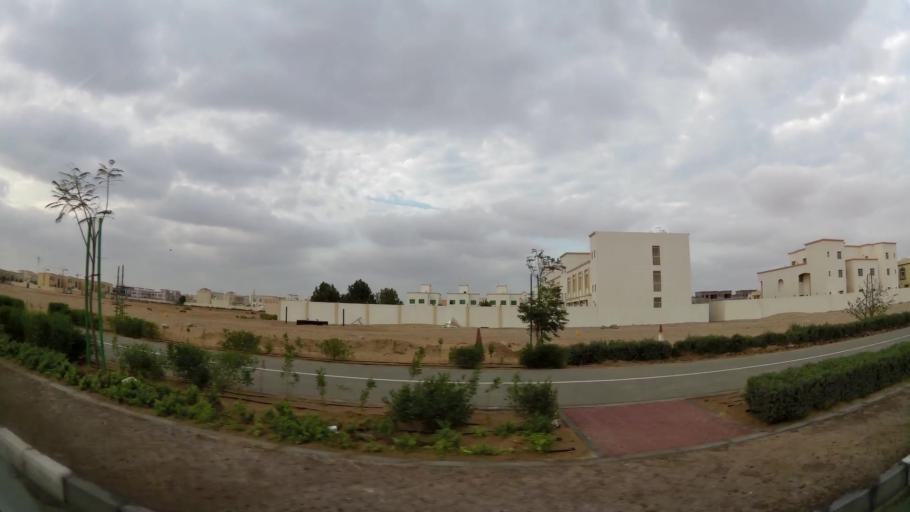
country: AE
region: Abu Dhabi
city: Abu Dhabi
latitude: 24.3478
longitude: 54.5494
